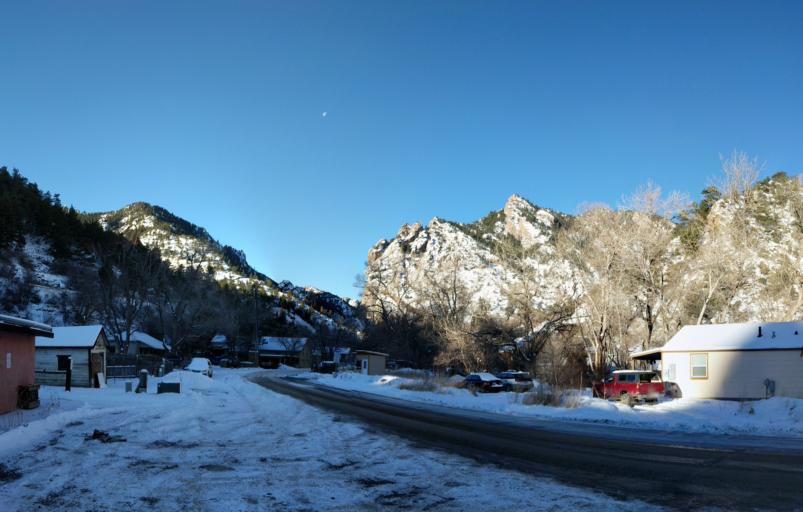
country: US
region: Colorado
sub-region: Boulder County
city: Boulder
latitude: 39.9331
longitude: -105.2738
